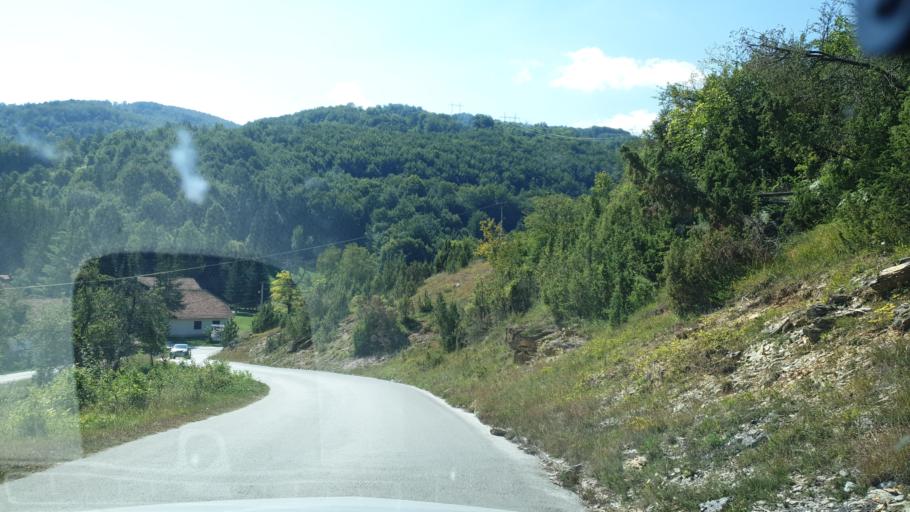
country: RS
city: Zlatibor
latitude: 43.6548
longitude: 19.8295
